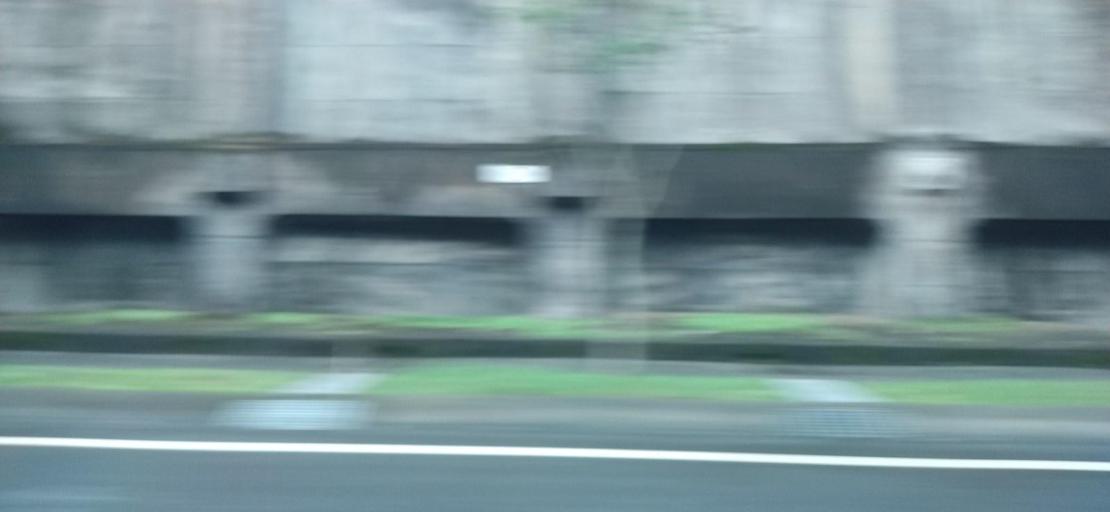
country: TW
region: Taiwan
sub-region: Yilan
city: Yilan
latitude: 24.6094
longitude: 121.8377
